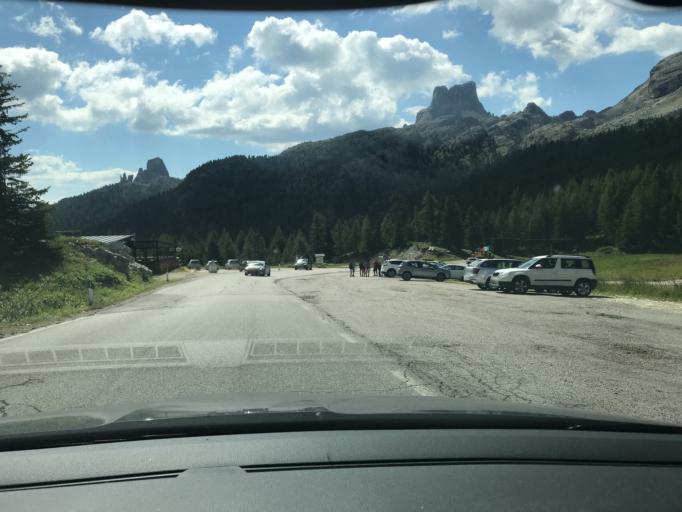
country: IT
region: Veneto
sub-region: Provincia di Belluno
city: Colle Santa Lucia
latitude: 46.5206
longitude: 12.0181
